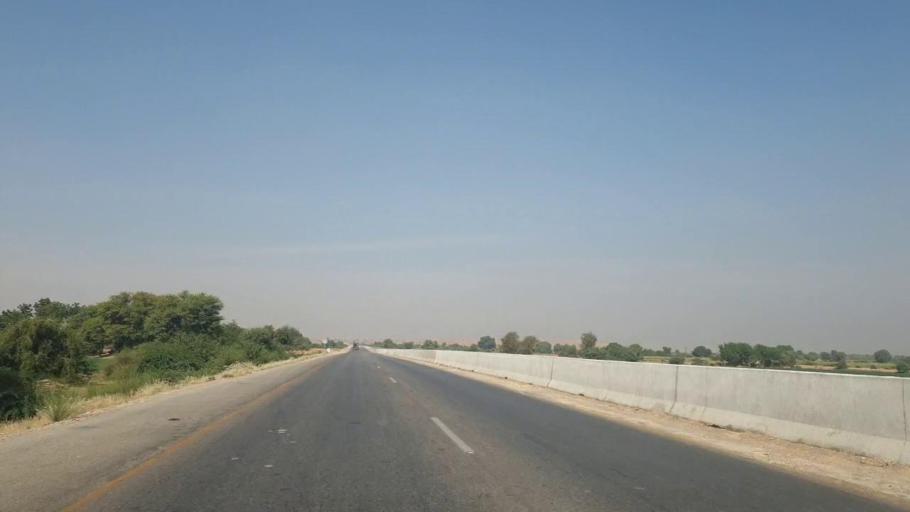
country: PK
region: Sindh
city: Matiari
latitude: 25.5944
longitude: 68.3086
